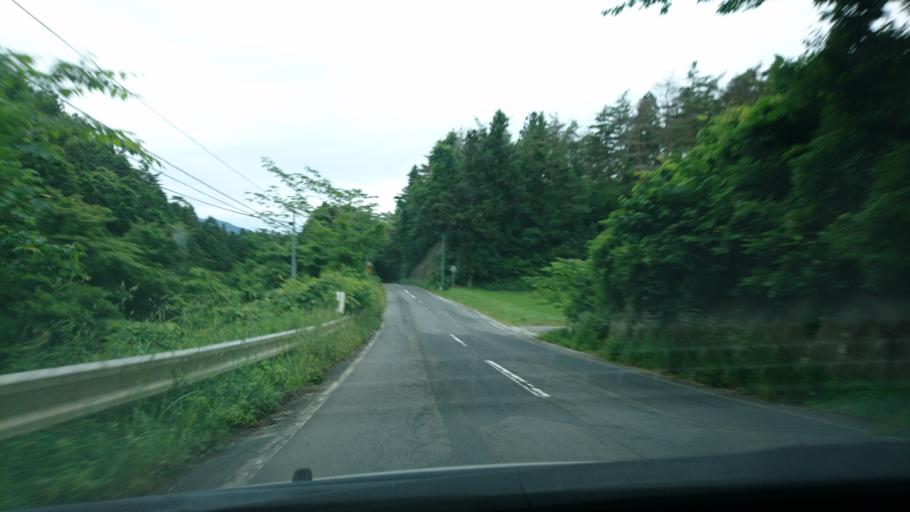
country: JP
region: Iwate
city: Ichinoseki
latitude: 38.9489
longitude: 141.2658
